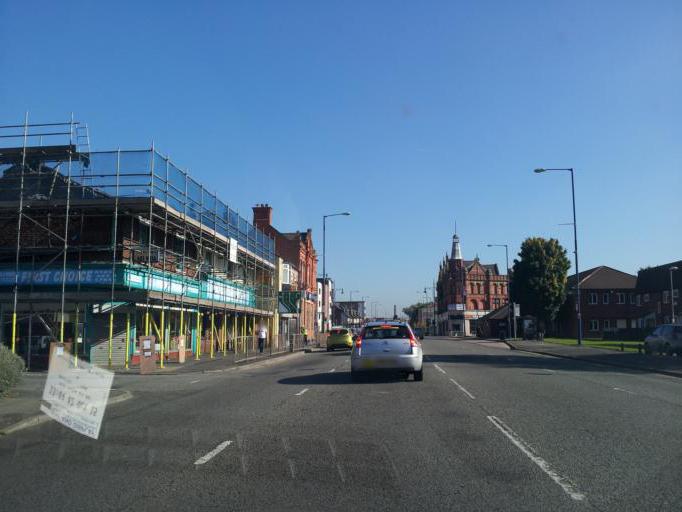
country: GB
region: England
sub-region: Manchester
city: Failsworth
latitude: 53.5025
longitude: -2.1858
